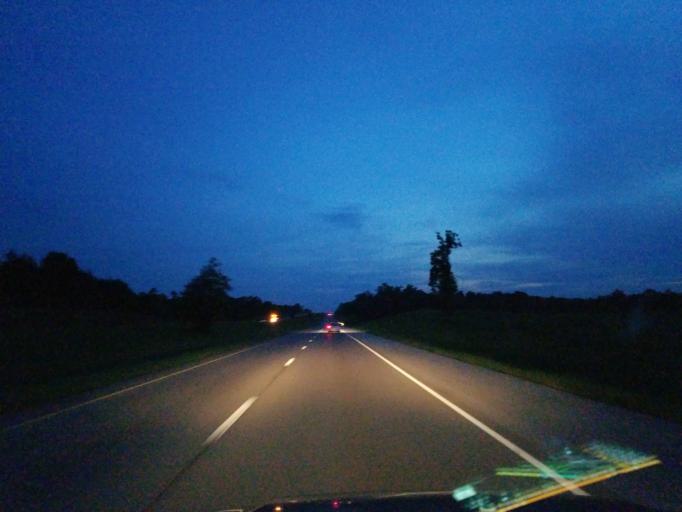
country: US
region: Mississippi
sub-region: Jones County
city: Ellisville
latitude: 31.5493
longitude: -89.2655
